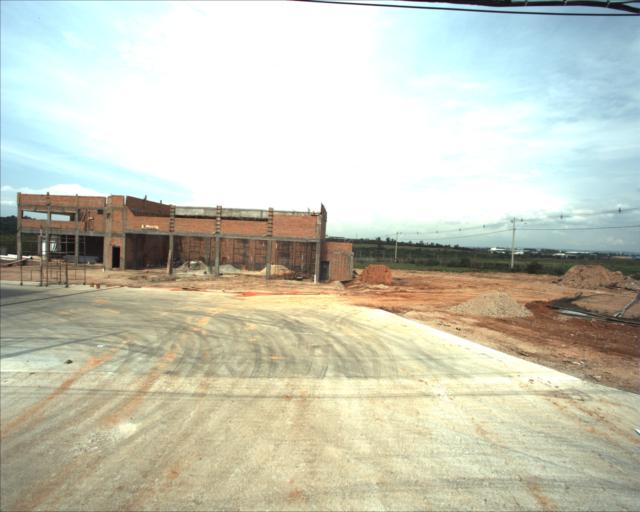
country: BR
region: Sao Paulo
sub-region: Sorocaba
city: Sorocaba
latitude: -23.4346
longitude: -47.4368
